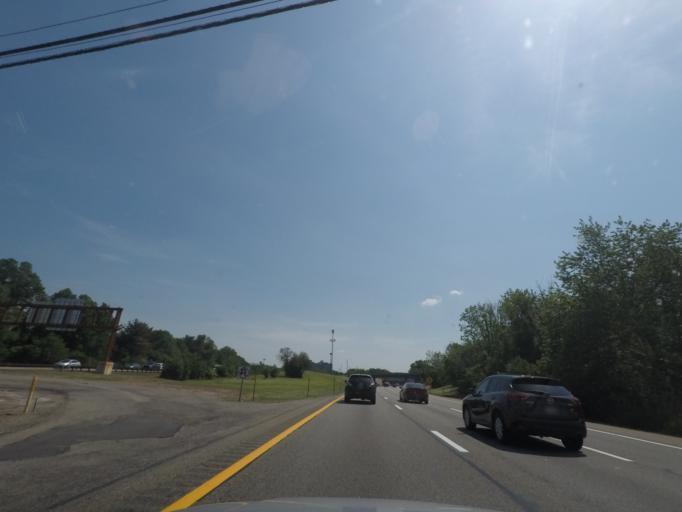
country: US
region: New Jersey
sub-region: Passaic County
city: Clifton
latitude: 40.8580
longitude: -74.1743
